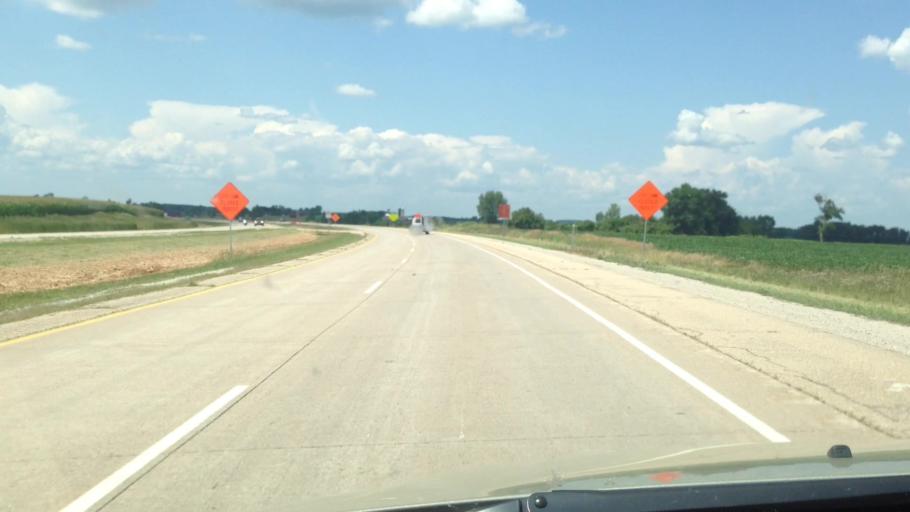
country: US
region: Wisconsin
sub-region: Brown County
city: Pulaski
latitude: 44.6830
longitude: -88.3126
